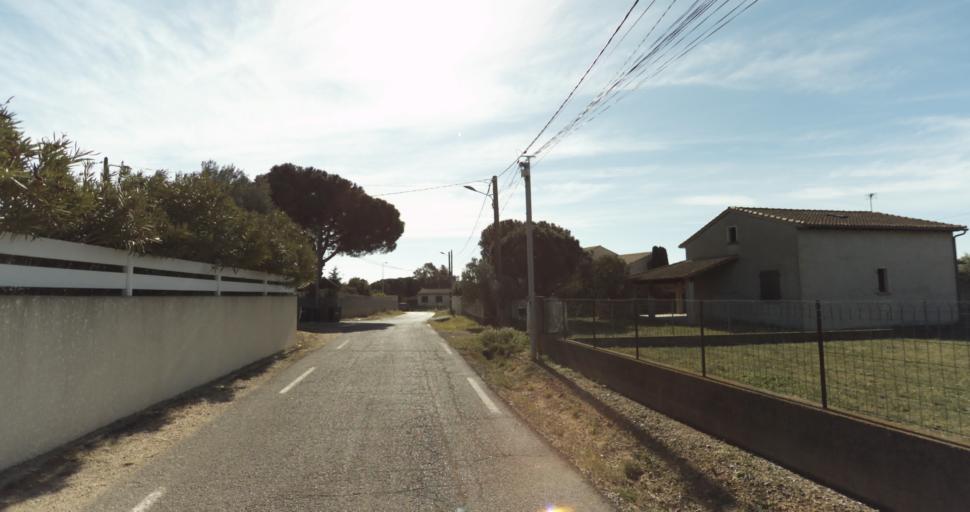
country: FR
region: Languedoc-Roussillon
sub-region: Departement de l'Herault
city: Marseillan
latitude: 43.3362
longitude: 3.5193
